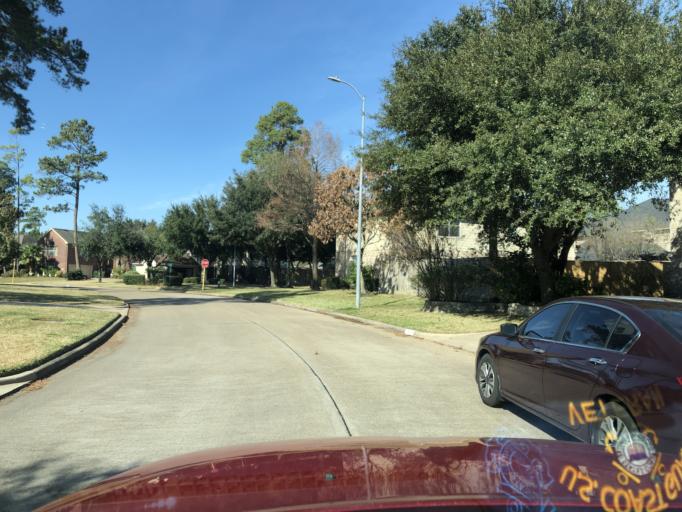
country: US
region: Texas
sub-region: Harris County
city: Tomball
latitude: 30.0230
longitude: -95.5530
